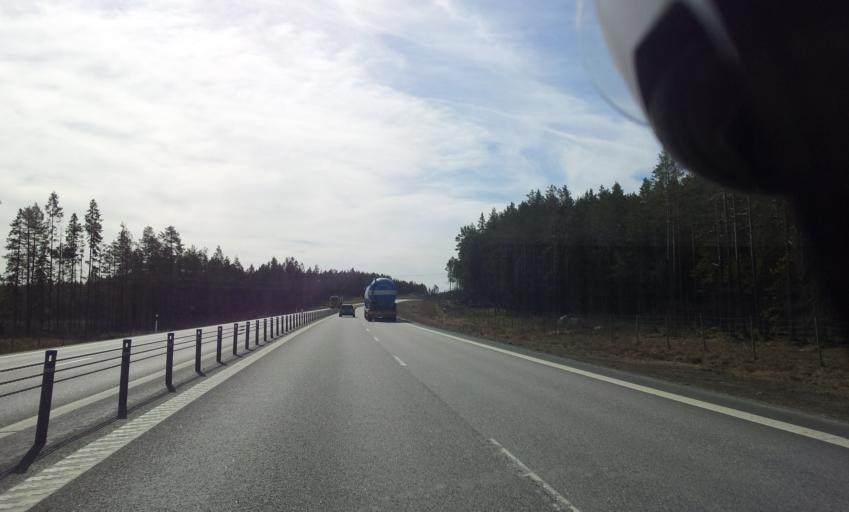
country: SE
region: Gaevleborg
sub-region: Hudiksvalls Kommun
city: Hudiksvall
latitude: 61.7005
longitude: 17.0549
